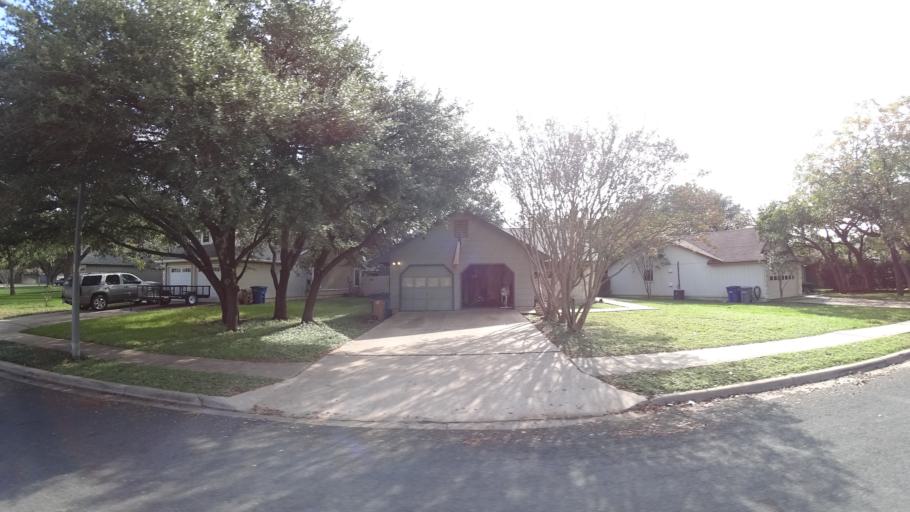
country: US
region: Texas
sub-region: Williamson County
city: Jollyville
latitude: 30.4307
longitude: -97.7286
